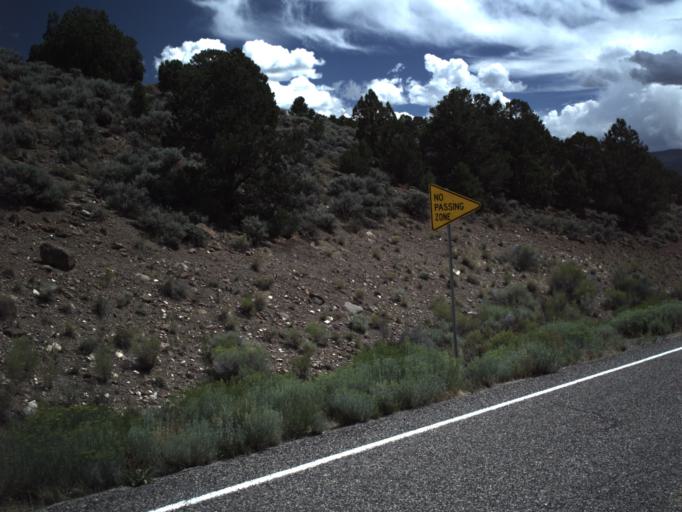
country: US
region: Utah
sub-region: Piute County
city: Junction
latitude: 38.2587
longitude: -112.2731
